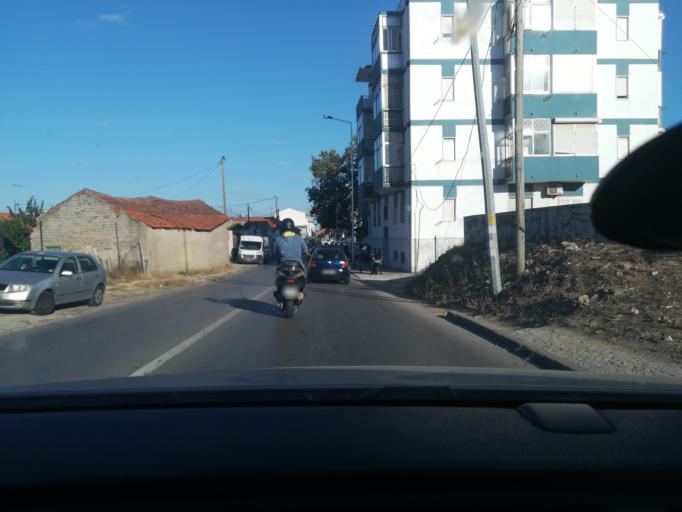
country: PT
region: Setubal
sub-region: Seixal
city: Corroios
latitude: 38.6455
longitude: -9.1594
